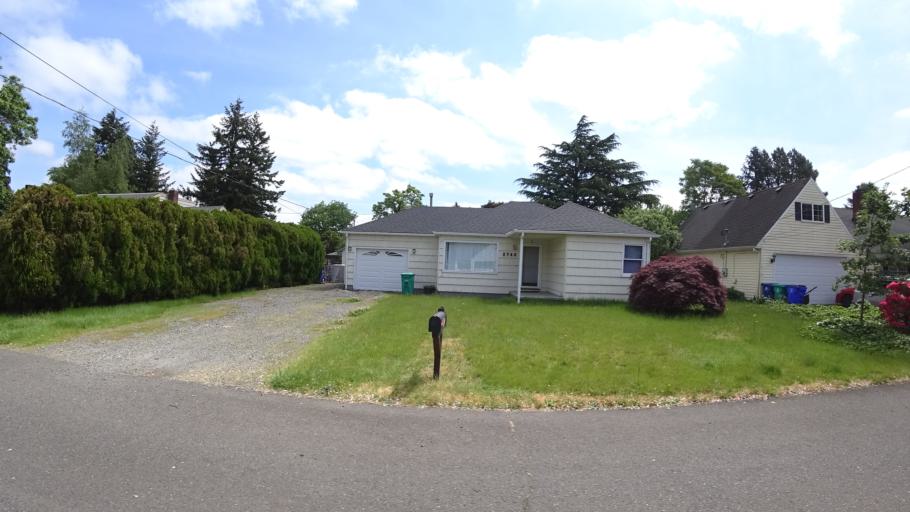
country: US
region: Oregon
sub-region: Multnomah County
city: Gresham
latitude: 45.5025
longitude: -122.4937
